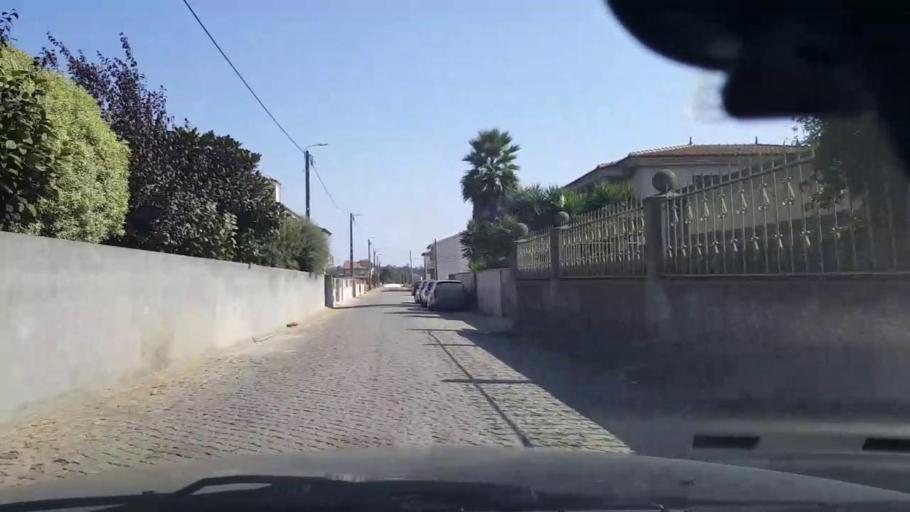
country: PT
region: Porto
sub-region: Povoa de Varzim
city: Pedroso
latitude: 41.4132
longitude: -8.6996
